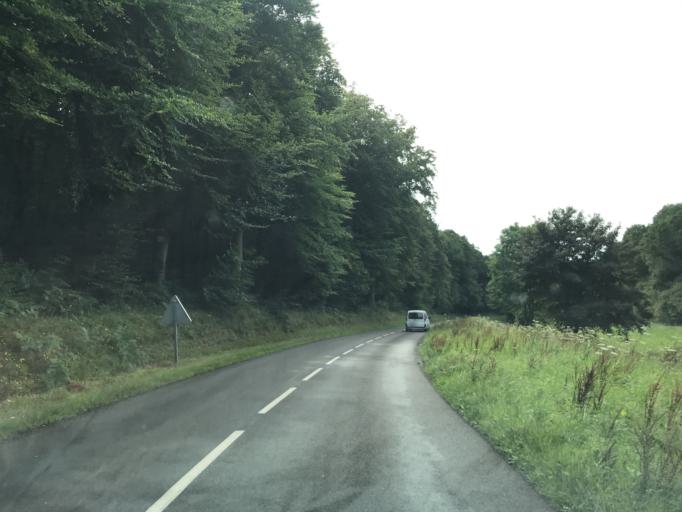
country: FR
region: Haute-Normandie
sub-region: Departement de la Seine-Maritime
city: Yport
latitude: 49.7317
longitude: 0.3335
